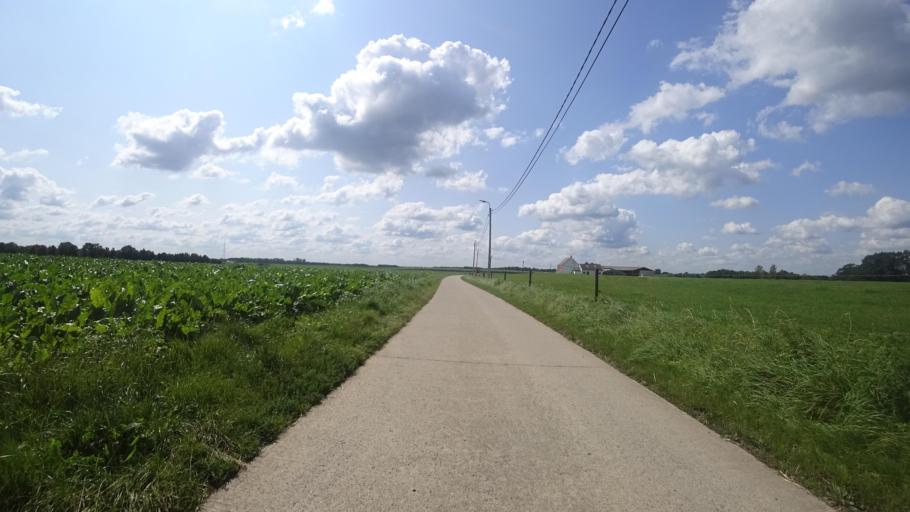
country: BE
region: Flanders
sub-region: Provincie Vlaams-Brabant
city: Huldenberg
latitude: 50.7776
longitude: 4.5898
